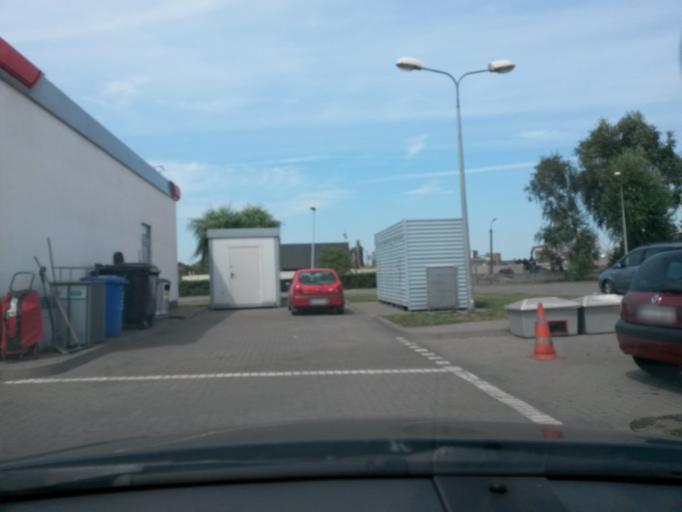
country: PL
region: Greater Poland Voivodeship
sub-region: Powiat sremski
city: Srem
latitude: 52.0682
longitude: 17.0375
